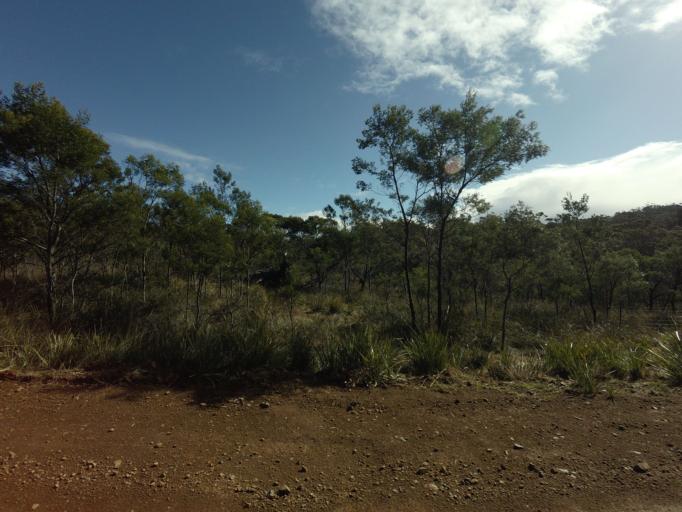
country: AU
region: Tasmania
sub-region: Sorell
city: Sorell
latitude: -42.4067
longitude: 147.9548
